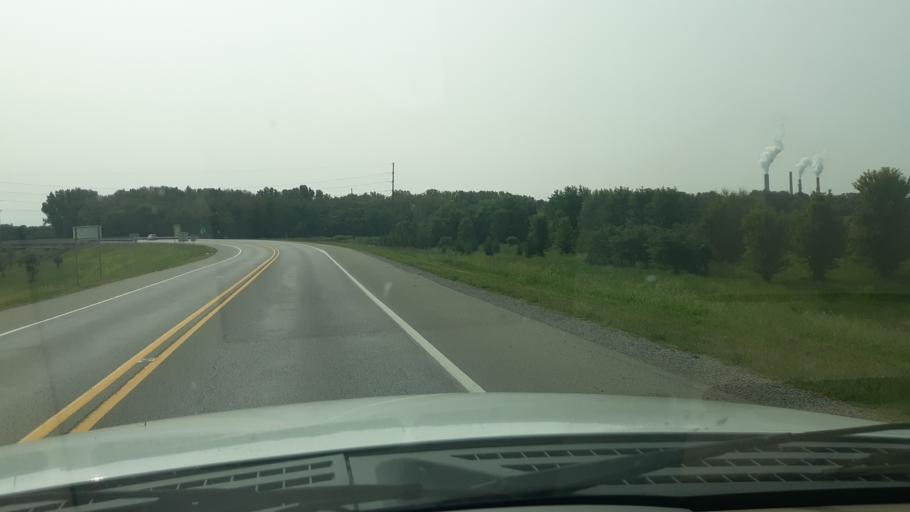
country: US
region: Illinois
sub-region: Wabash County
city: Mount Carmel
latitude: 38.4018
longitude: -87.7603
